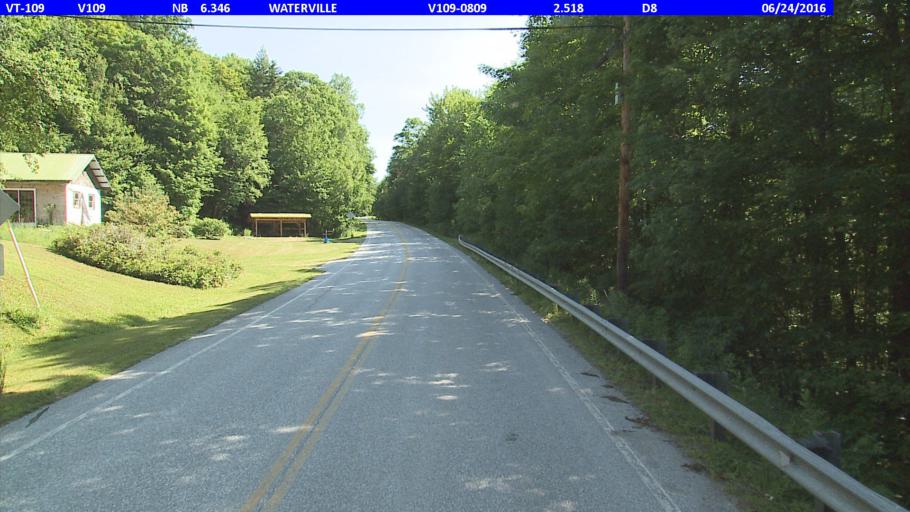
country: US
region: Vermont
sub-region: Lamoille County
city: Johnson
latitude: 44.7146
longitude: -72.7543
